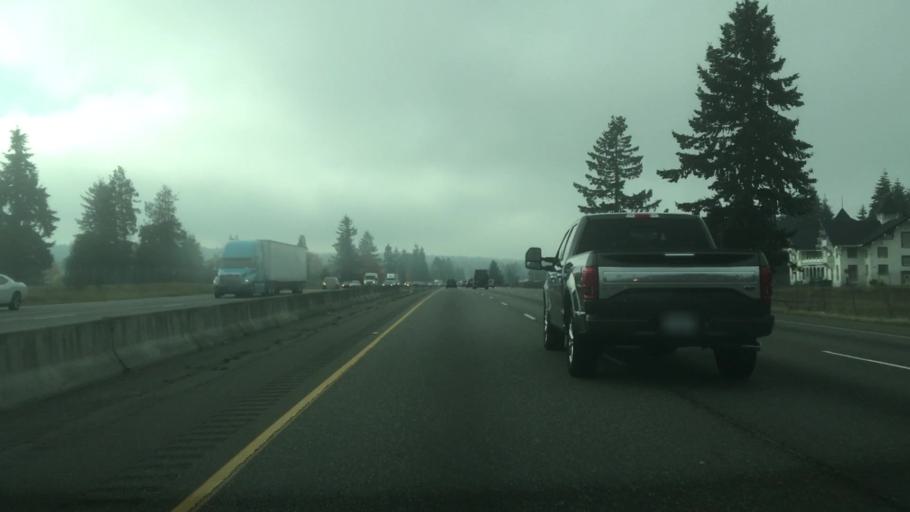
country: US
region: Washington
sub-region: Pierce County
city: DuPont
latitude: 47.0975
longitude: -122.6127
